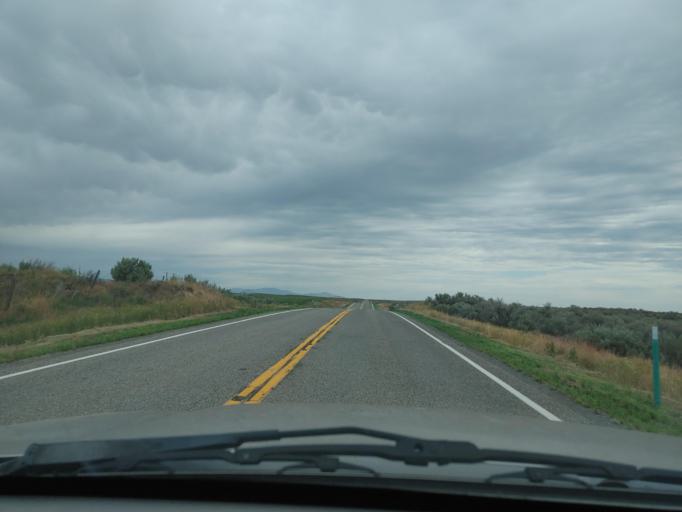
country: US
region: Idaho
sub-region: Lincoln County
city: Shoshone
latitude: 43.0602
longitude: -114.1278
